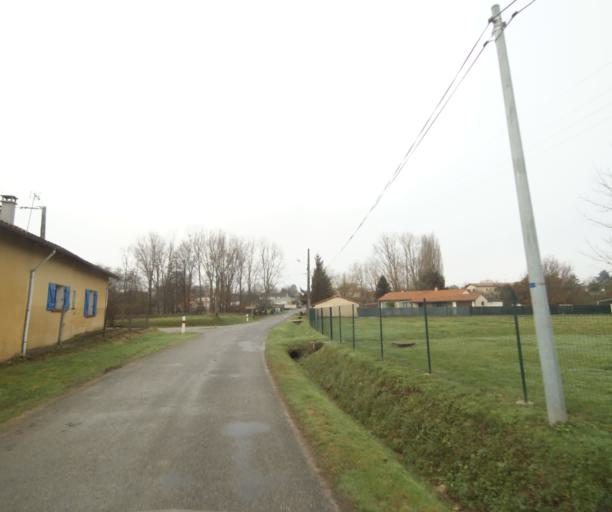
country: FR
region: Midi-Pyrenees
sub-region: Departement du Tarn-et-Garonne
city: Nohic
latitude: 43.8773
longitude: 1.4675
